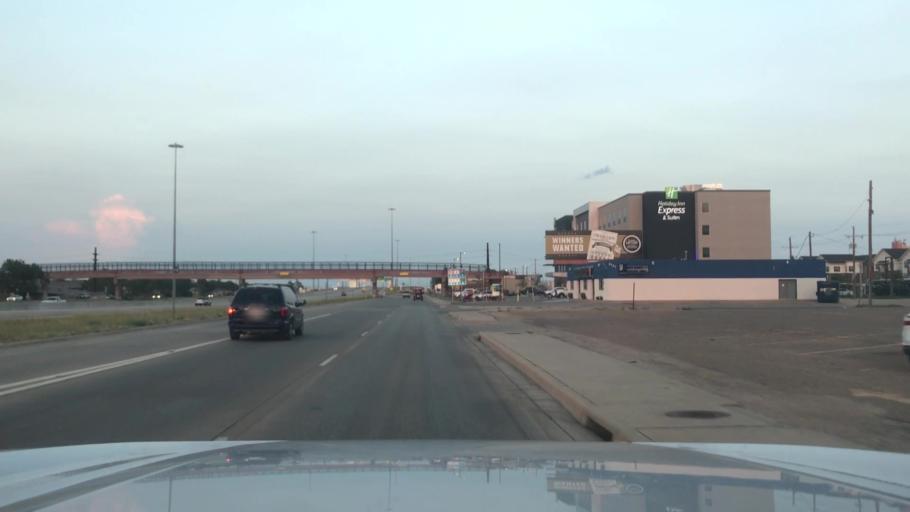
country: US
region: Texas
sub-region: Lubbock County
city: Lubbock
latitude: 33.5922
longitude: -101.8648
